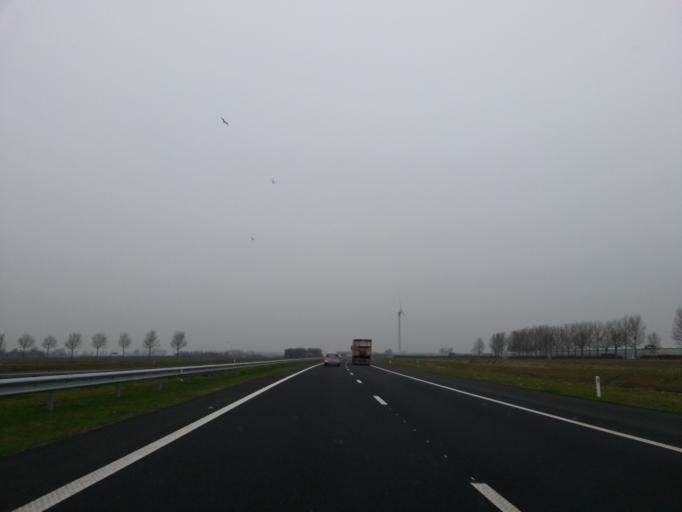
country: NL
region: North Brabant
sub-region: Gemeente Bergen op Zoom
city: Lepelstraat
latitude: 51.5660
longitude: 4.2859
